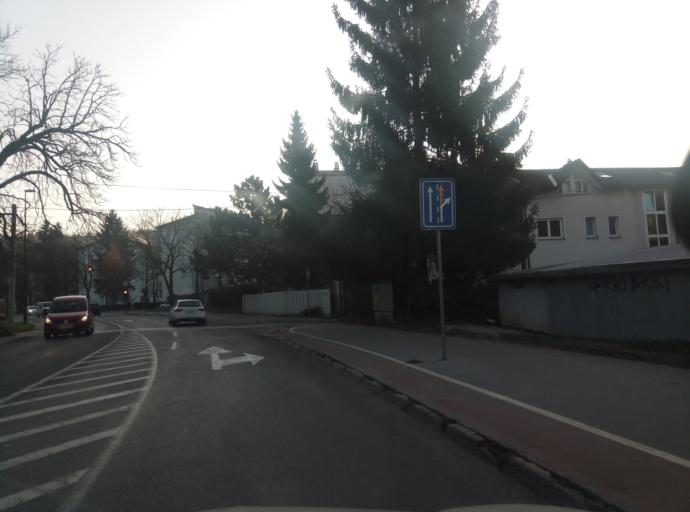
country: SI
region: Ljubljana
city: Ljubljana
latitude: 46.0527
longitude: 14.5390
